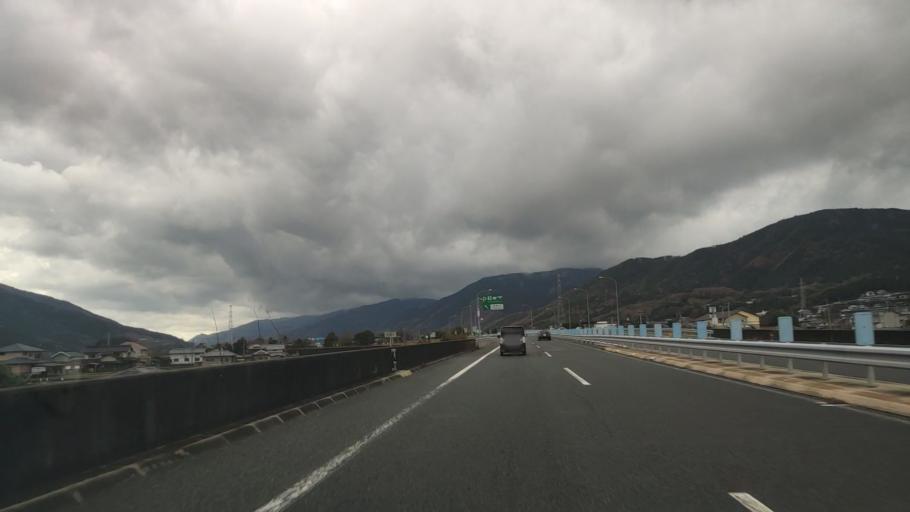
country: JP
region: Tokushima
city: Ikedacho
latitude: 34.0371
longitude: 133.8988
